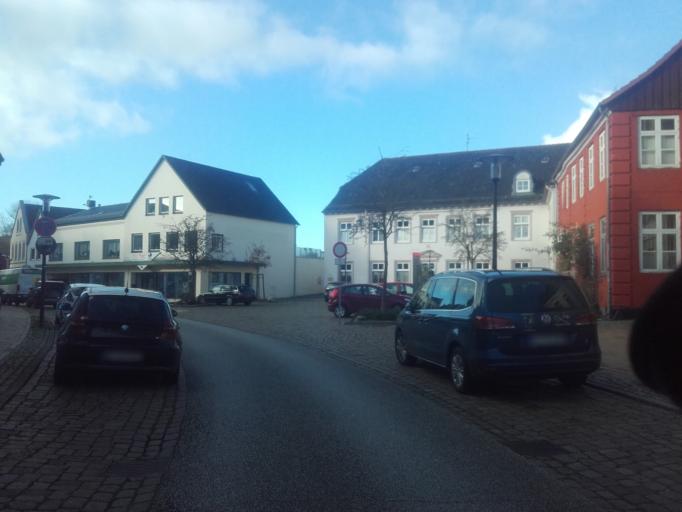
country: DE
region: Schleswig-Holstein
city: Busdorf
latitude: 54.5023
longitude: 9.5440
